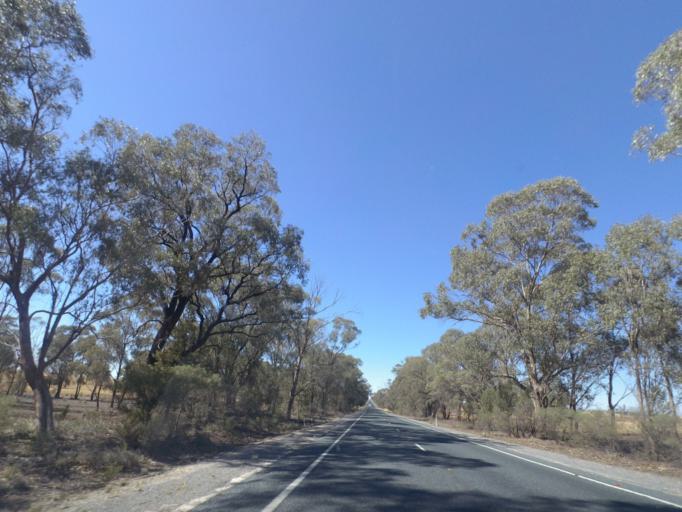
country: AU
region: New South Wales
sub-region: Bland
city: West Wyalong
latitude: -34.1475
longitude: 147.1190
